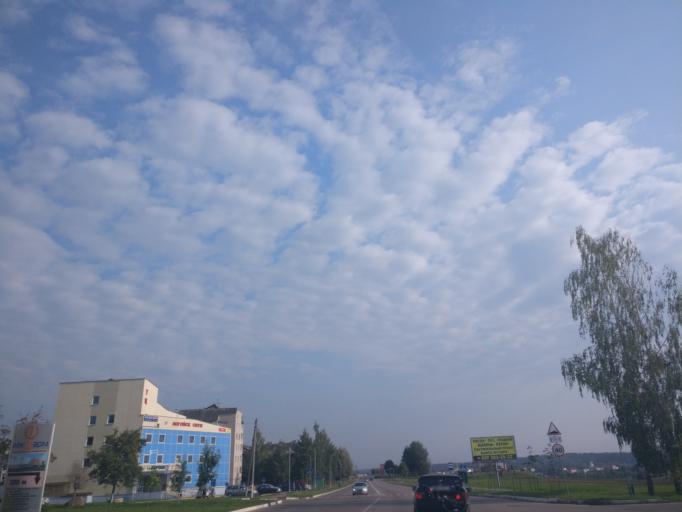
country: BY
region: Minsk
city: Lahoysk
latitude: 54.1910
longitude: 27.8306
